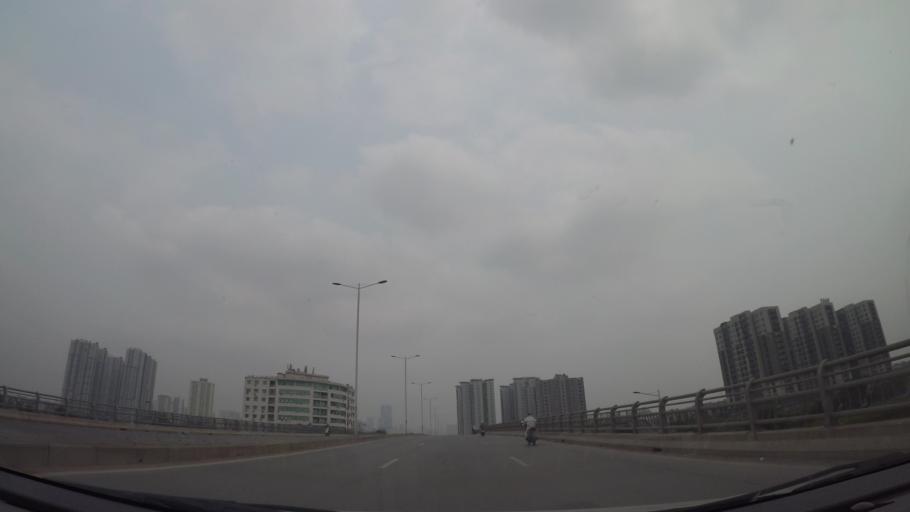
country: VN
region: Ha Noi
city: Cau Dien
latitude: 21.0347
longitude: 105.7519
